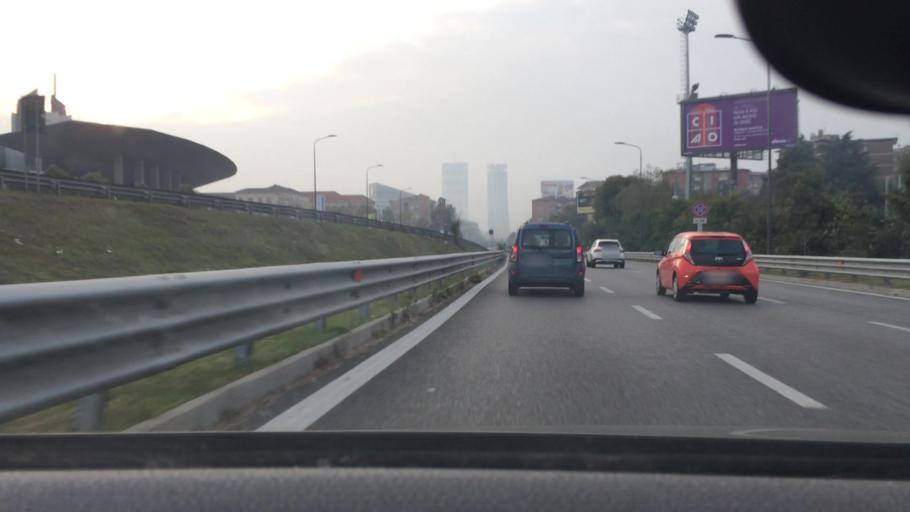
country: IT
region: Lombardy
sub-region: Citta metropolitana di Milano
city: Novate Milanese
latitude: 45.4904
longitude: 9.1385
